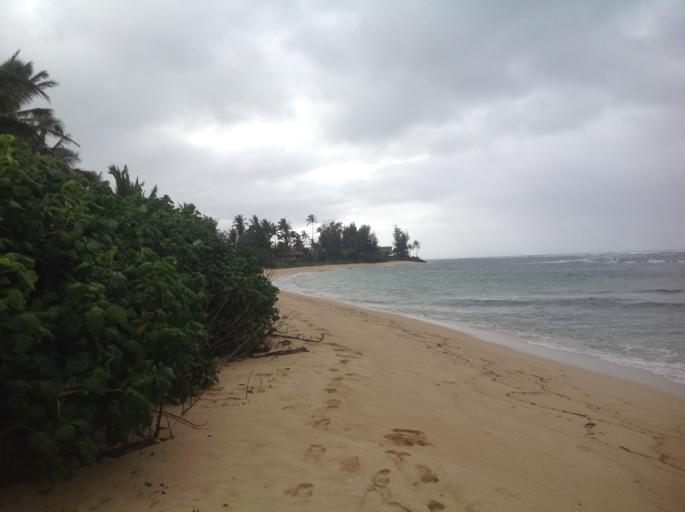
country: US
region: Hawaii
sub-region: Honolulu County
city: Waialua
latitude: 21.5824
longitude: -158.1306
